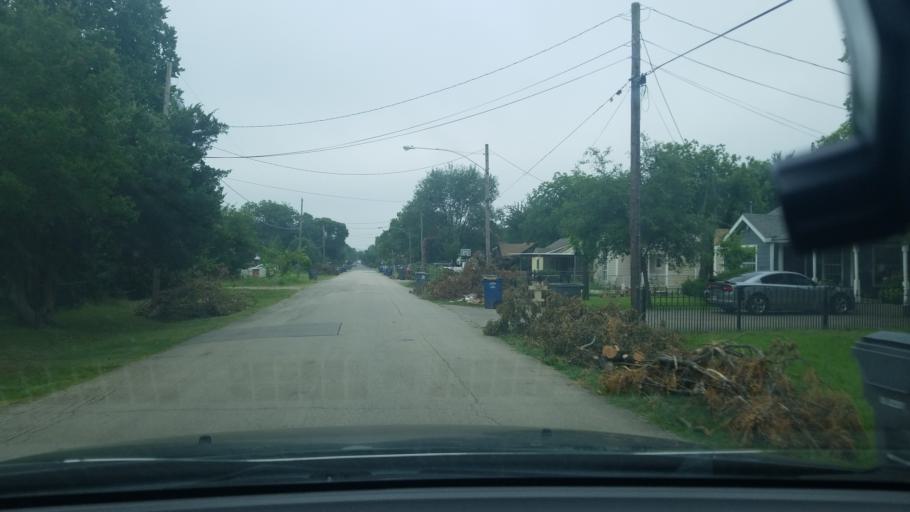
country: US
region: Texas
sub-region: Dallas County
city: Balch Springs
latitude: 32.7594
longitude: -96.6801
